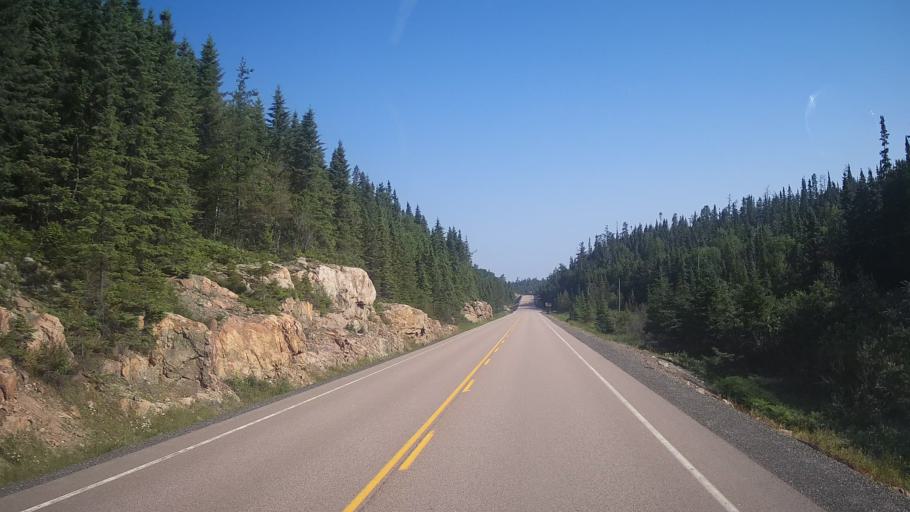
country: CA
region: Ontario
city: Rayside-Balfour
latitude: 47.0014
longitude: -81.6326
